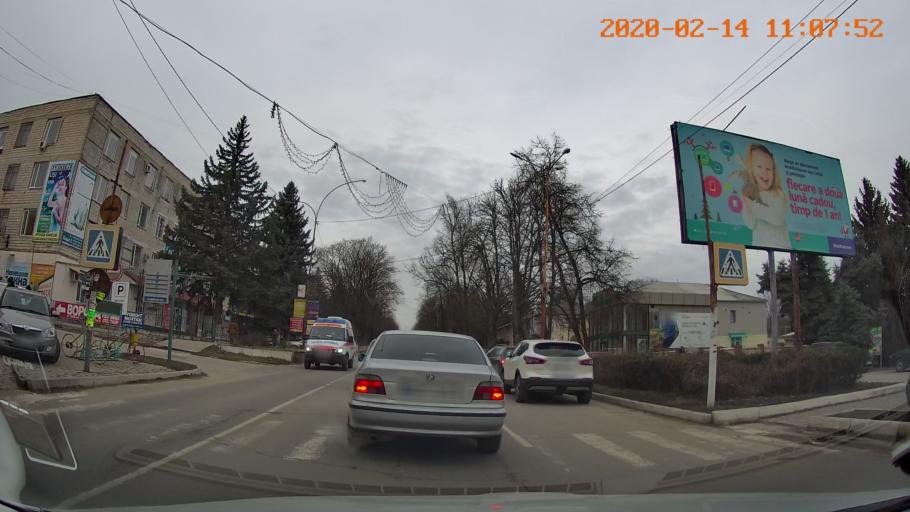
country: MD
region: Raionul Edinet
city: Edinet
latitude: 48.1703
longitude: 27.3048
